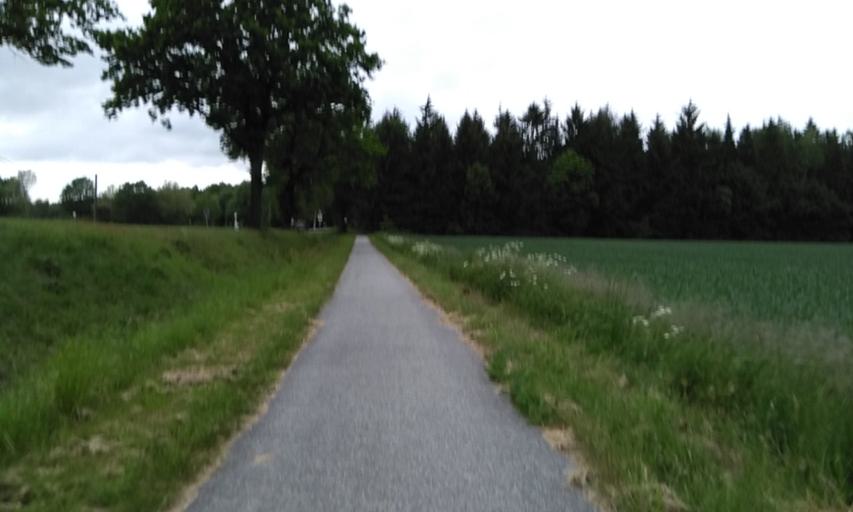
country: DE
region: Lower Saxony
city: Harsefeld
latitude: 53.4912
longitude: 9.4928
